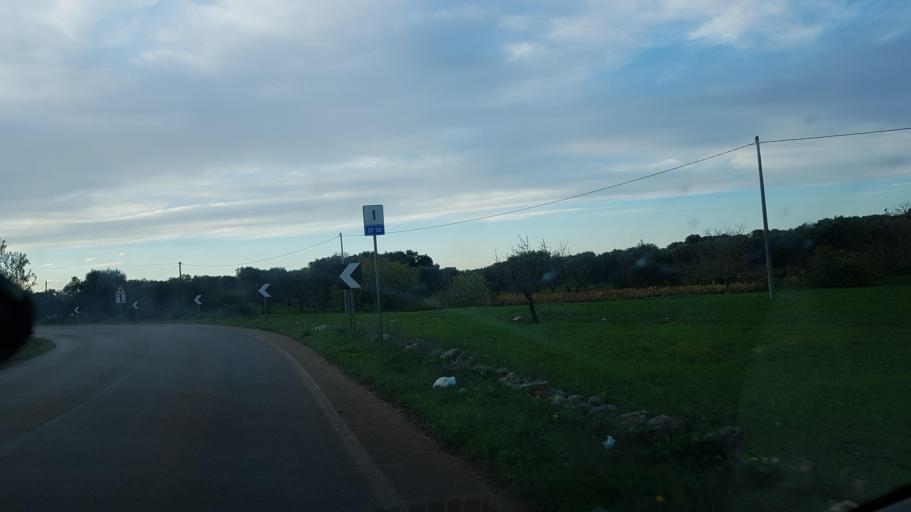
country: IT
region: Apulia
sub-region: Provincia di Brindisi
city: San Vito dei Normanni
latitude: 40.6487
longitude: 17.6832
